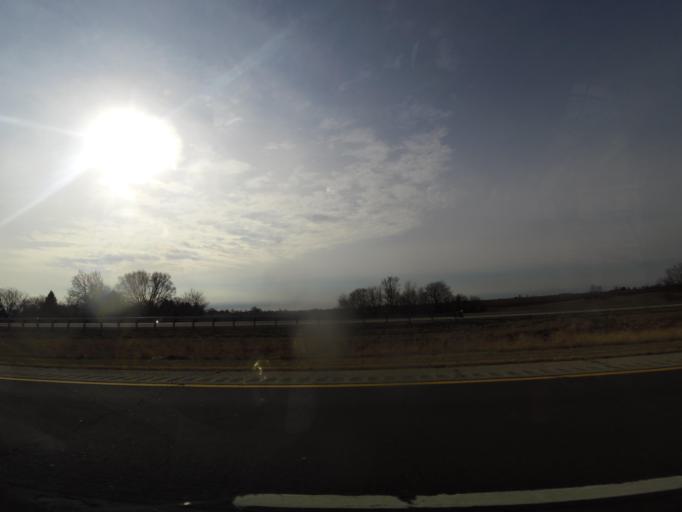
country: US
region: Illinois
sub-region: Macon County
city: Decatur
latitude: 39.7869
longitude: -88.9819
